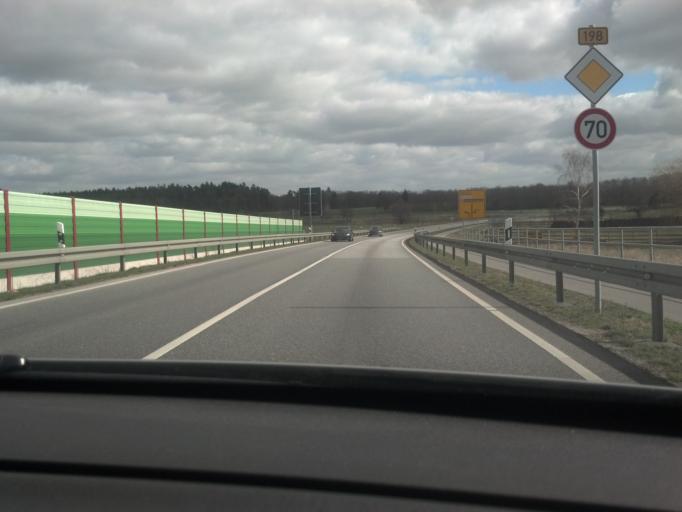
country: DE
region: Mecklenburg-Vorpommern
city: Malchow
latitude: 53.3680
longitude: 12.4709
